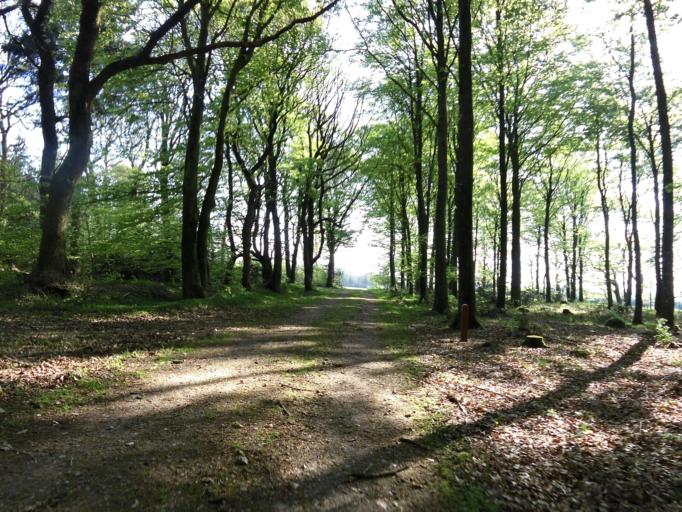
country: DK
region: South Denmark
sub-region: Tonder Kommune
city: Toftlund
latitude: 55.1971
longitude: 8.9379
